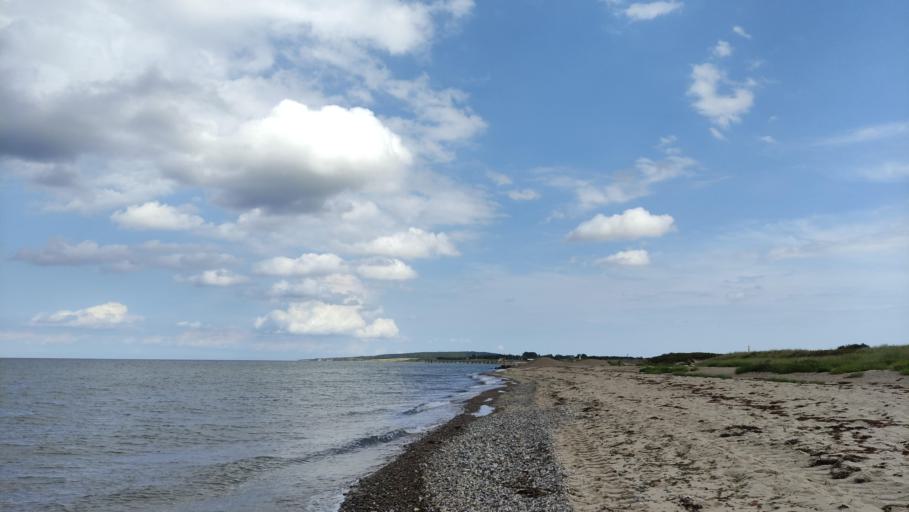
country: DE
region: Schleswig-Holstein
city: Wangels
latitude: 54.3096
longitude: 10.7800
